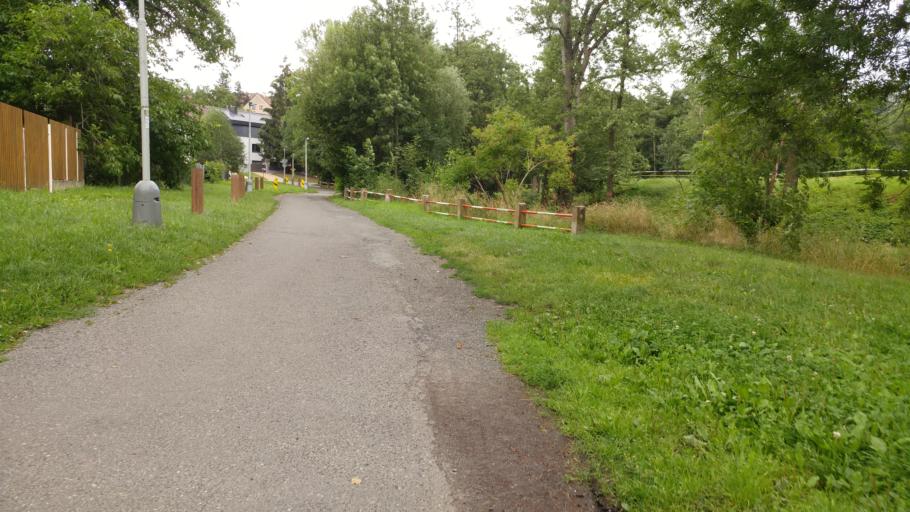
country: CZ
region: Praha
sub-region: Praha 14
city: Hostavice
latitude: 50.0495
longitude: 14.5316
